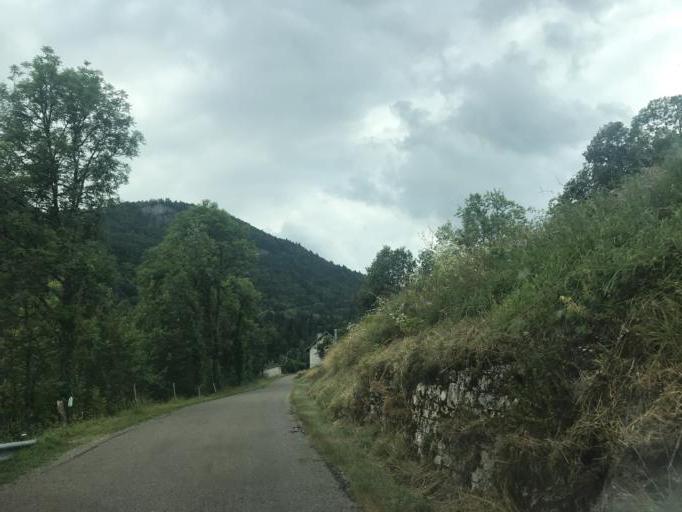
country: FR
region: Franche-Comte
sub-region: Departement du Jura
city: Saint-Claude
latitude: 46.3452
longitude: 5.8363
